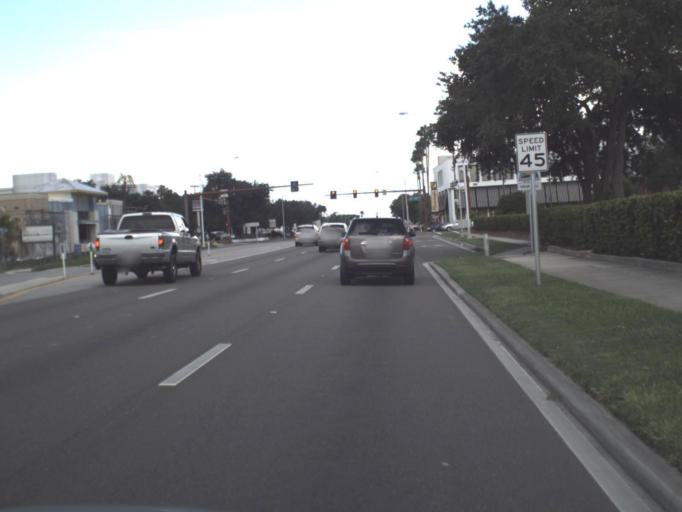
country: US
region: Florida
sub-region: Sarasota County
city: South Sarasota
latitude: 27.3016
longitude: -82.5303
